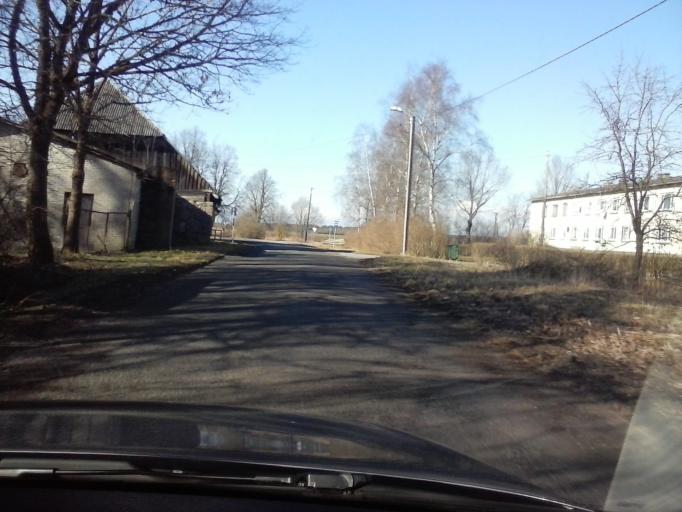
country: EE
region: Tartu
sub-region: Noo vald
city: Noo
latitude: 58.3130
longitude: 26.5475
